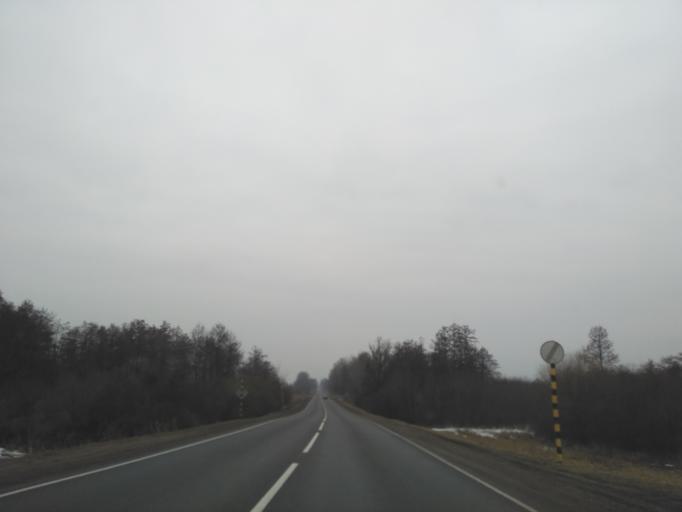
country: BY
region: Brest
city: Baranovichi
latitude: 53.2075
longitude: 26.1147
